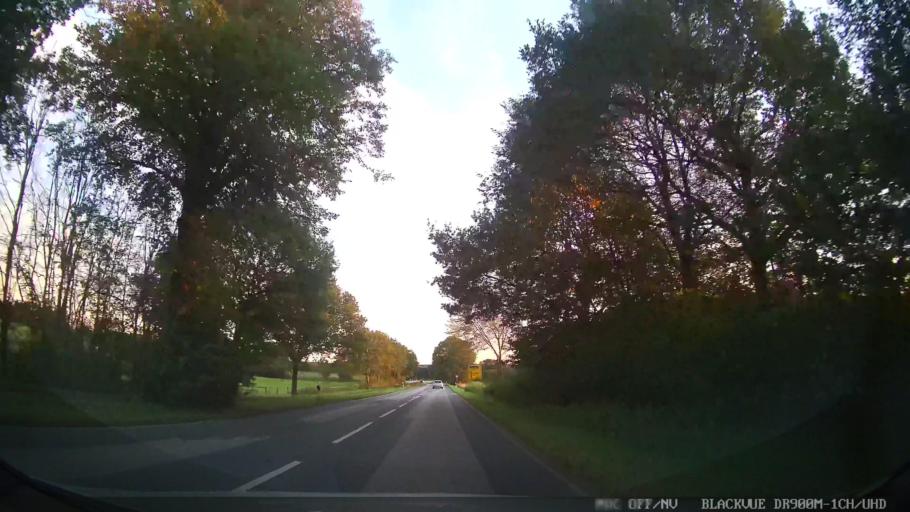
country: DE
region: Schleswig-Holstein
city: Susel
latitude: 54.0162
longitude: 10.6868
